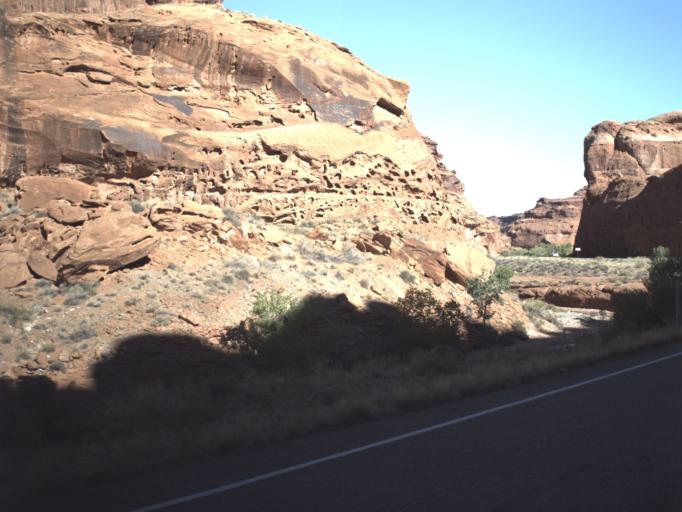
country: US
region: Utah
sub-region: San Juan County
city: Blanding
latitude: 37.9668
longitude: -110.4919
